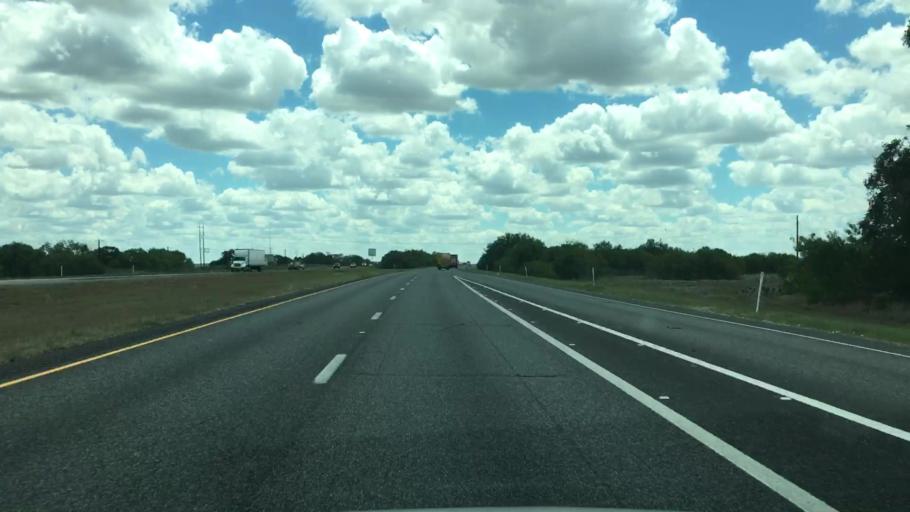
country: US
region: Texas
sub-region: Atascosa County
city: Pleasanton
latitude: 28.9430
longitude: -98.4366
